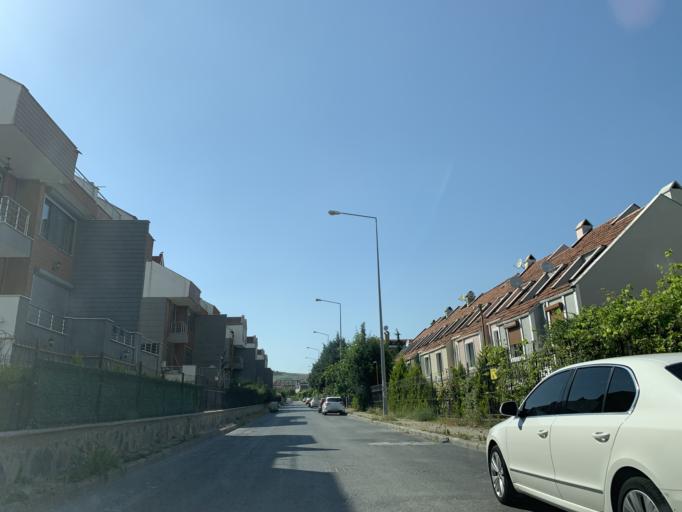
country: TR
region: Istanbul
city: Esenyurt
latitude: 41.0824
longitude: 28.6760
